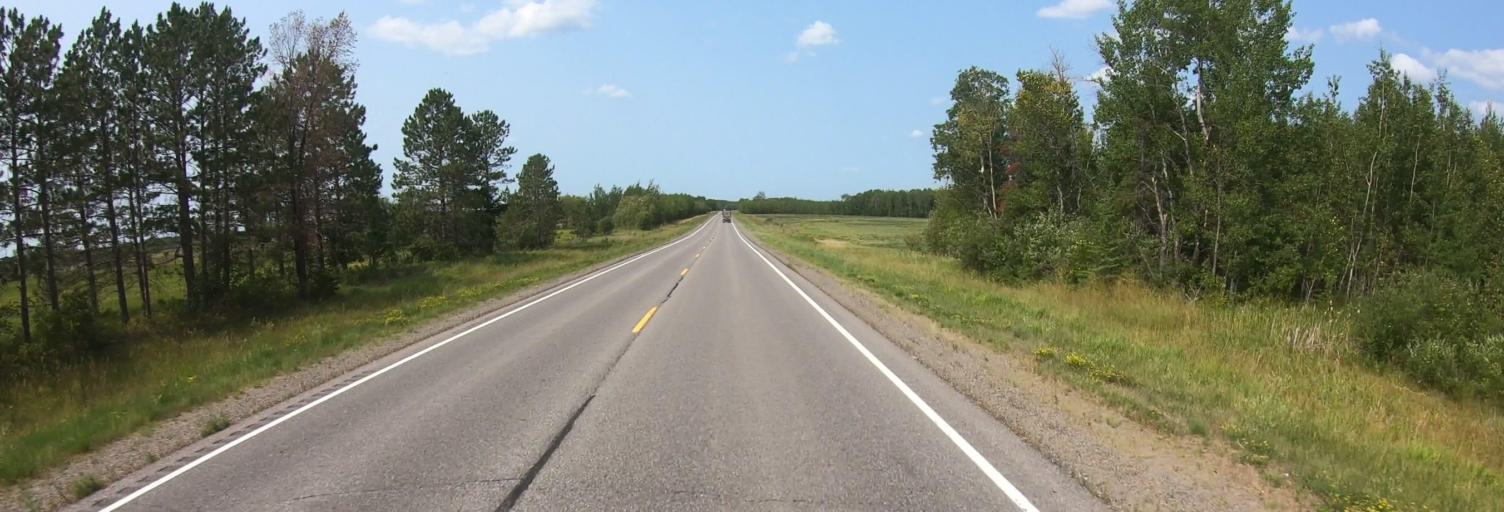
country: US
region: Minnesota
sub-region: Lake of the Woods County
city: Baudette
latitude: 48.6303
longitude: -94.1152
